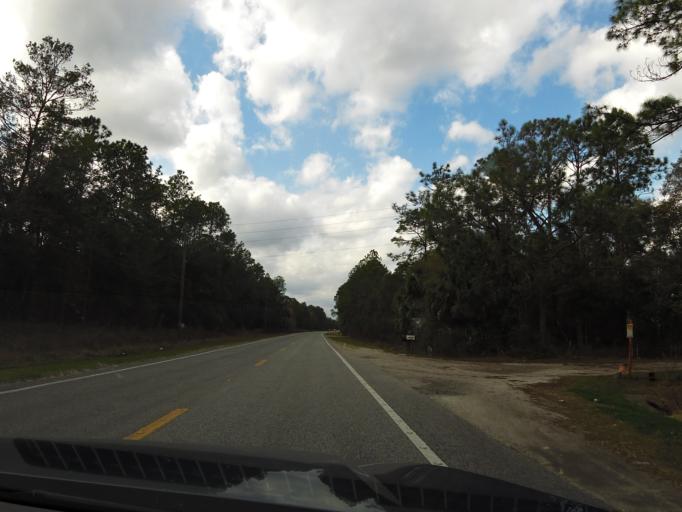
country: US
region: Florida
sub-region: Volusia County
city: Pierson
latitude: 29.1997
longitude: -81.4364
